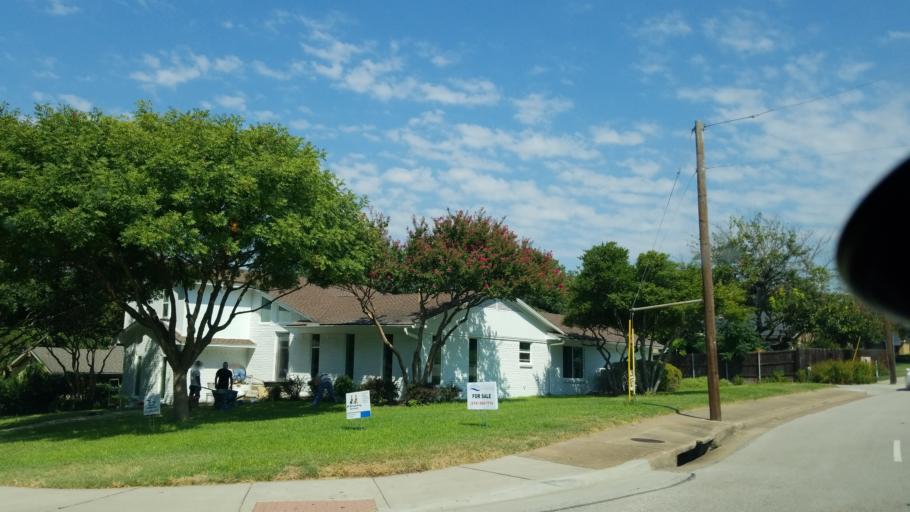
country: US
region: Texas
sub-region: Dallas County
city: Richardson
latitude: 32.8804
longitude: -96.7092
